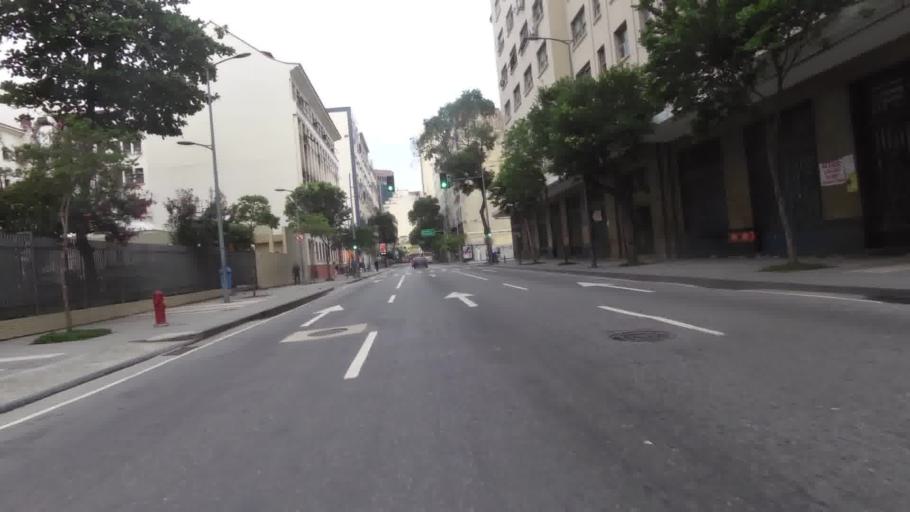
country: BR
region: Rio de Janeiro
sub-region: Rio De Janeiro
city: Rio de Janeiro
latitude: -22.8960
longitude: -43.1857
